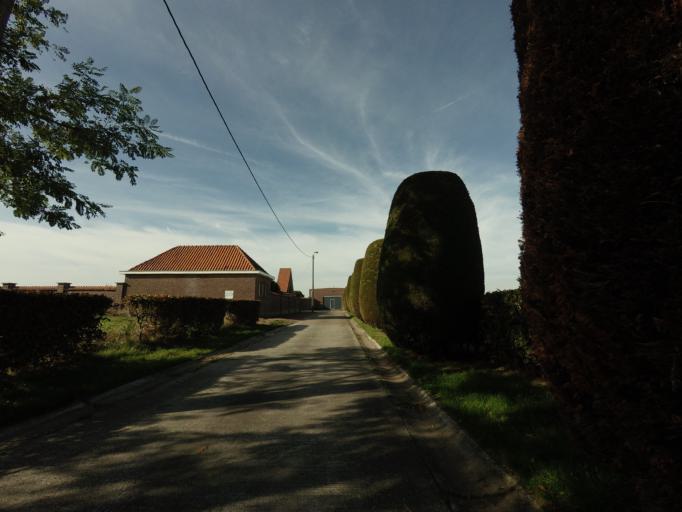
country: BE
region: Flanders
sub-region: Provincie Vlaams-Brabant
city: Kortenberg
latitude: 50.9075
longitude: 4.5621
